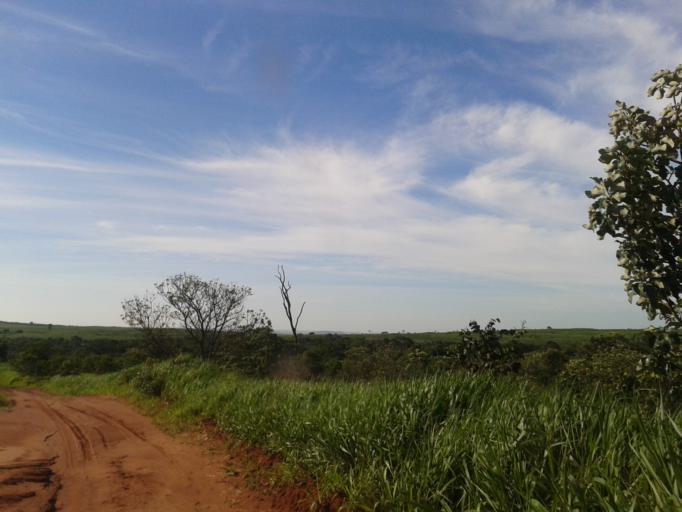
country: BR
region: Minas Gerais
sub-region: Santa Vitoria
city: Santa Vitoria
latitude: -19.1208
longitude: -49.9970
